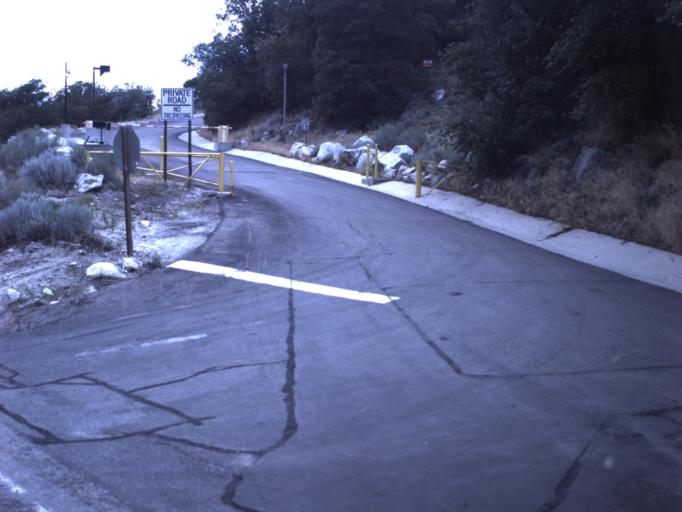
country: US
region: Utah
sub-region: Salt Lake County
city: Granite
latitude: 40.5720
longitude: -111.7585
